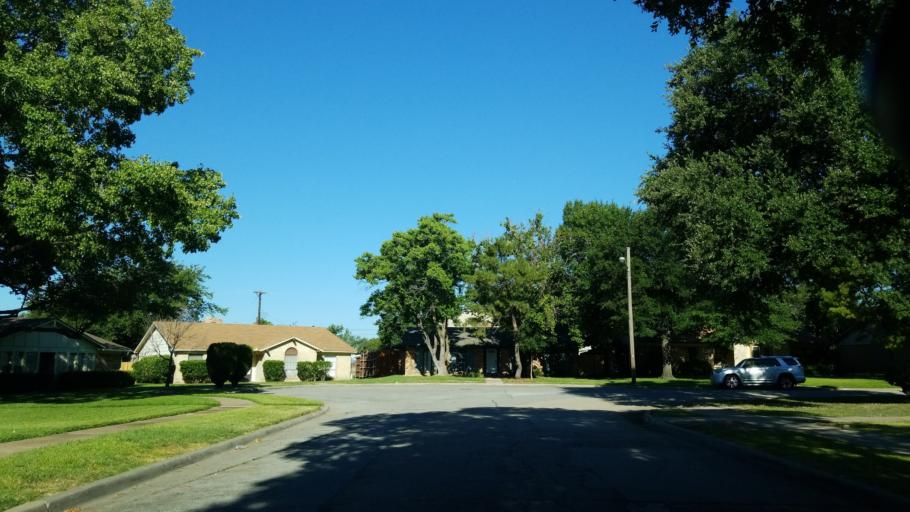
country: US
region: Texas
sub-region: Dallas County
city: Carrollton
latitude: 32.9423
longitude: -96.8877
